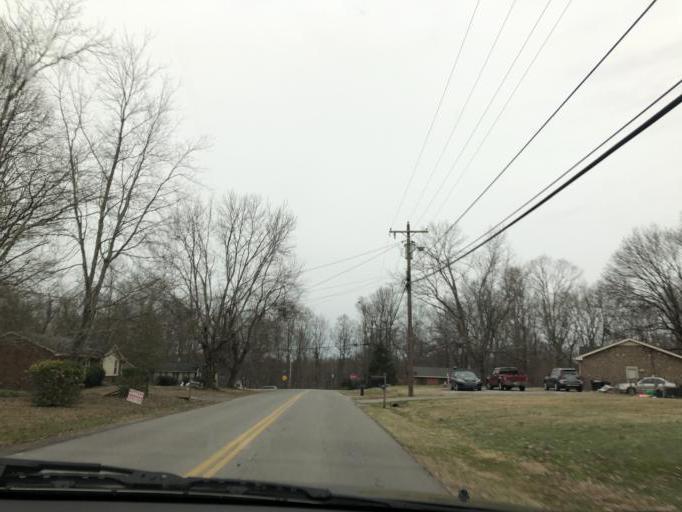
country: US
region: Tennessee
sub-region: Sumner County
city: White House
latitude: 36.4251
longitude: -86.6847
